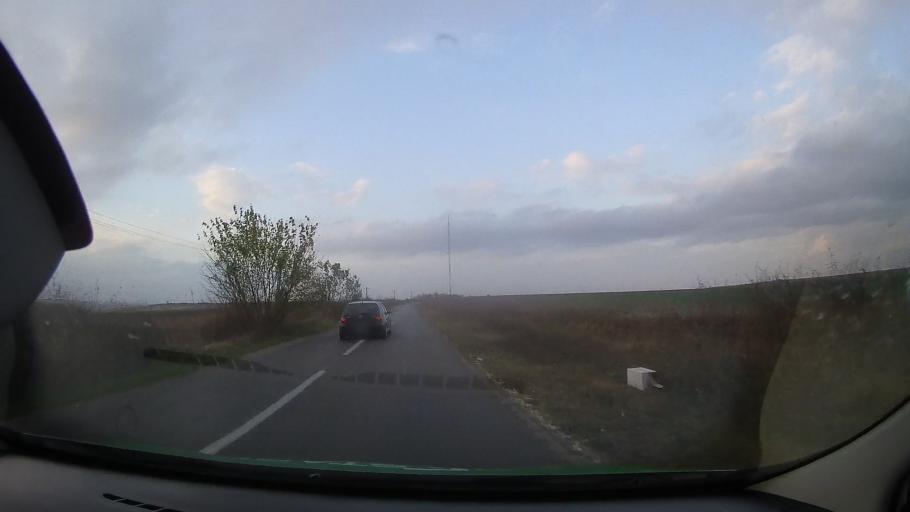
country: RO
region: Constanta
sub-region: Comuna Dobromir
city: Dobromir
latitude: 44.0416
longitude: 27.7562
